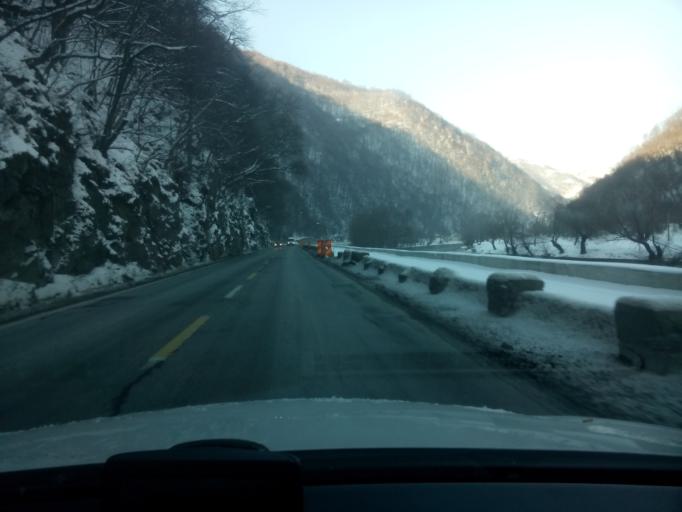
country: RO
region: Sibiu
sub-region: Comuna Boita
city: Boita
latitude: 45.5636
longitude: 24.2528
